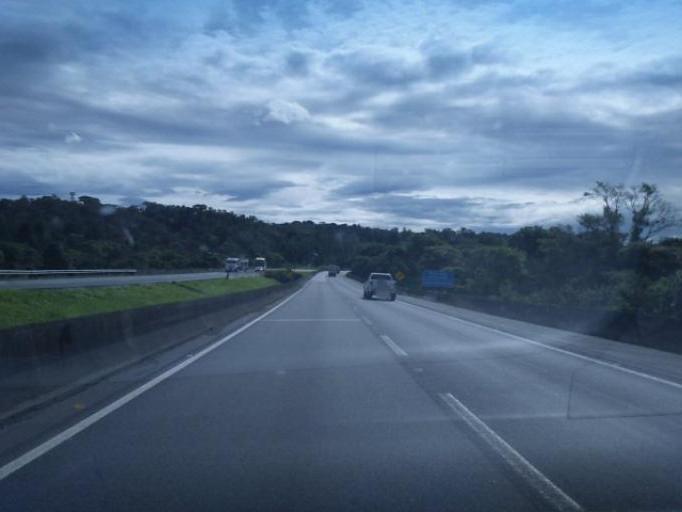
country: BR
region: Sao Paulo
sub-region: Cajati
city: Cajati
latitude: -24.9705
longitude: -48.3677
